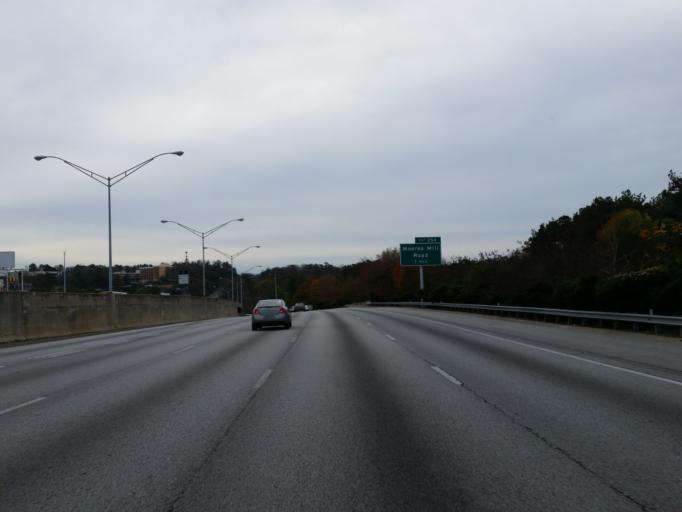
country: US
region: Georgia
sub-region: Cobb County
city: Vinings
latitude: 33.8502
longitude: -84.4311
